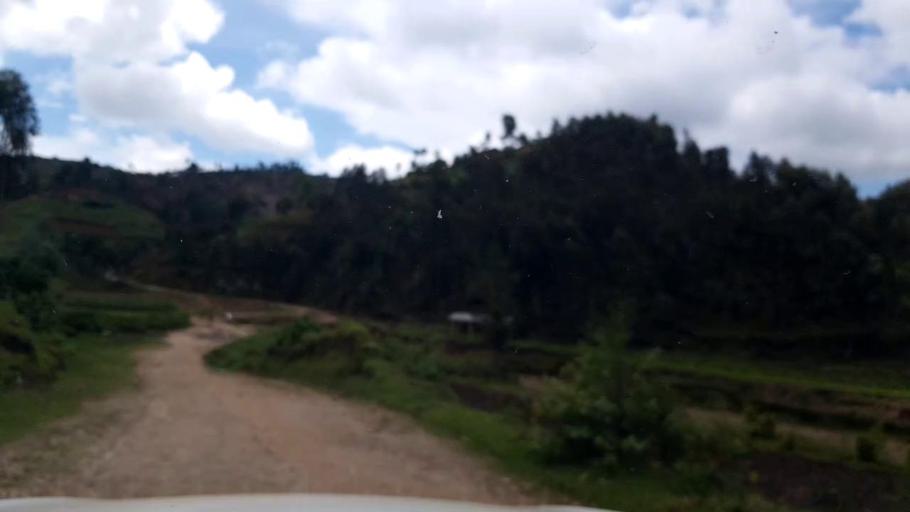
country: RW
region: Western Province
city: Kibuye
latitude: -1.9053
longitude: 29.4562
